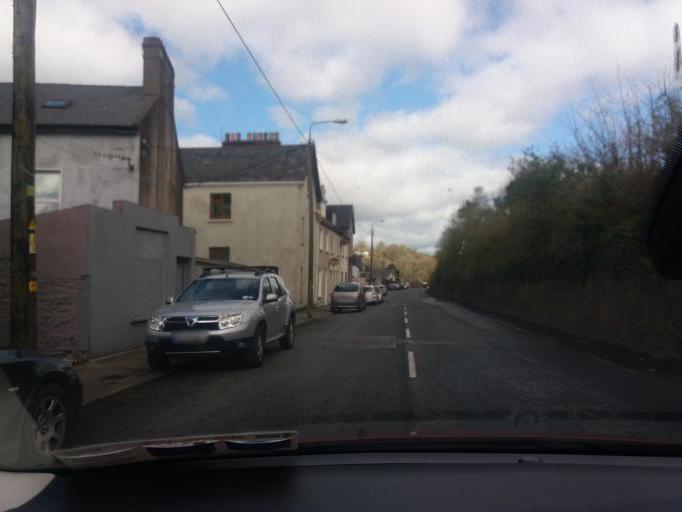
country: IE
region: Munster
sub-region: County Cork
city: Cobh
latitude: 51.8511
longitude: -8.3253
